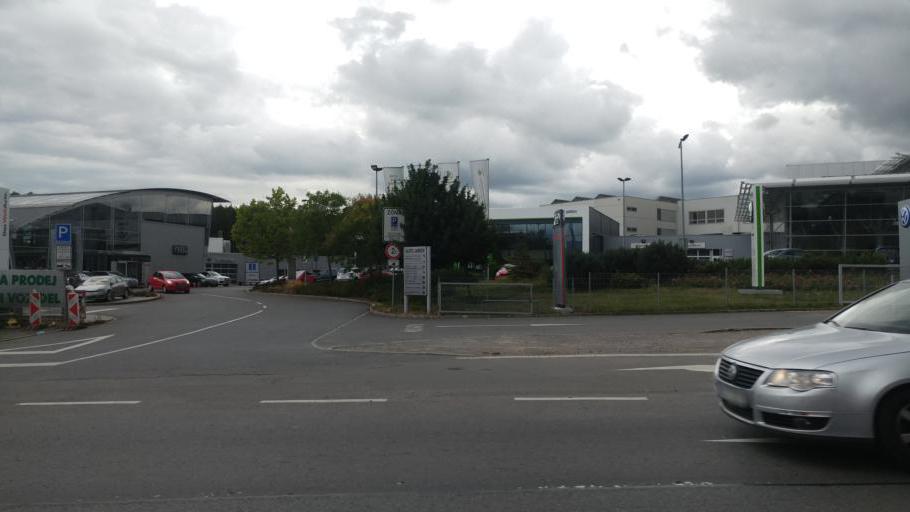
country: CZ
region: Praha
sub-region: Praha 9
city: Vysocany
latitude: 50.0908
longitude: 14.5012
